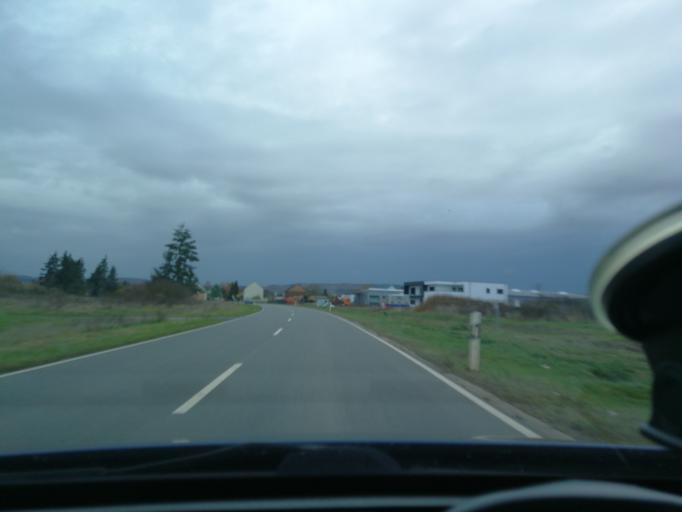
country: DE
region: Rheinland-Pfalz
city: Platten
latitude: 49.9664
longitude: 6.9425
